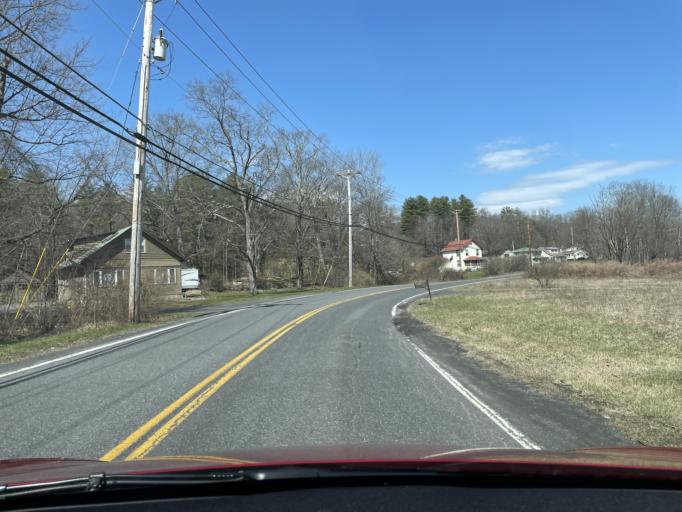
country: US
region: New York
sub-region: Ulster County
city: Manorville
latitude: 42.0848
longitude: -74.0142
